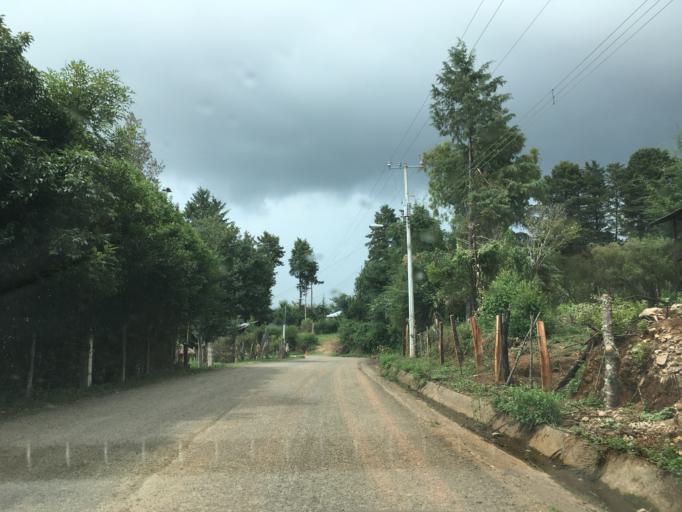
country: MX
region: Michoacan
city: Acuitzio del Canje
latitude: 19.5081
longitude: -101.2157
